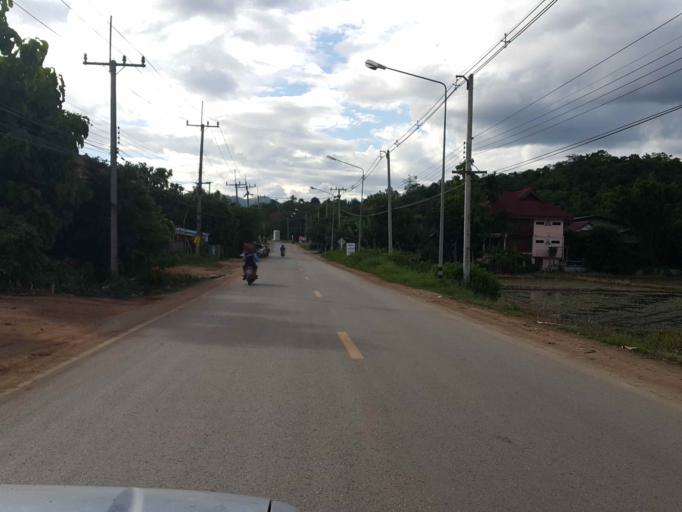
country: TH
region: Chiang Mai
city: Mae Chaem
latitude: 18.4924
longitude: 98.3762
